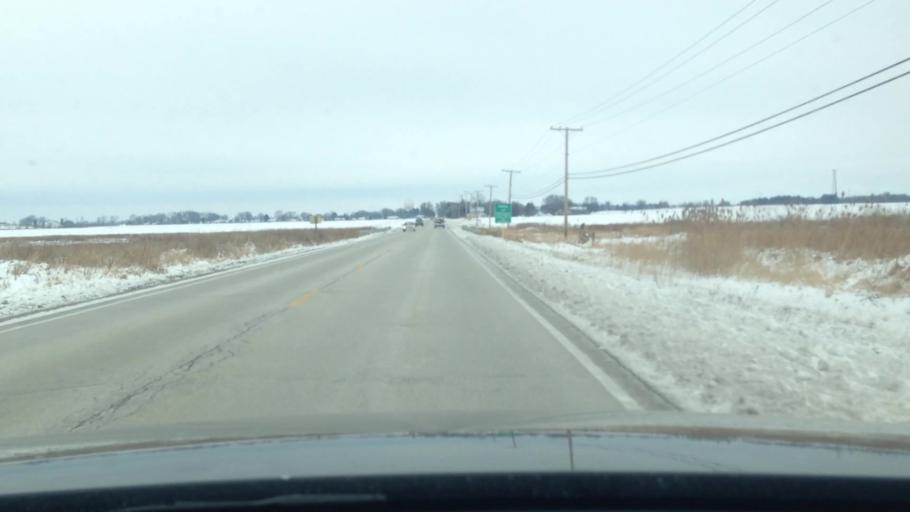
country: US
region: Illinois
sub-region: McHenry County
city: Hebron
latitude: 42.4499
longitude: -88.4330
